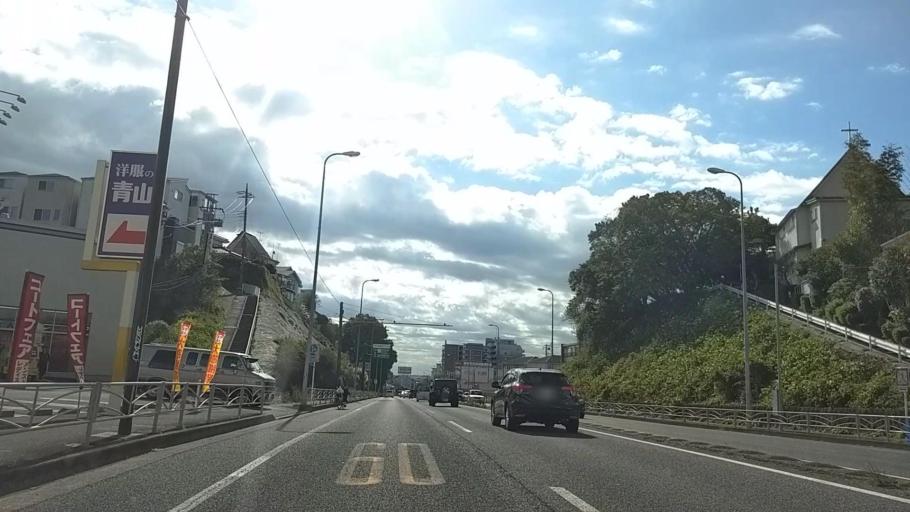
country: JP
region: Kanagawa
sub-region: Kawasaki-shi
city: Kawasaki
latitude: 35.5046
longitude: 139.6621
